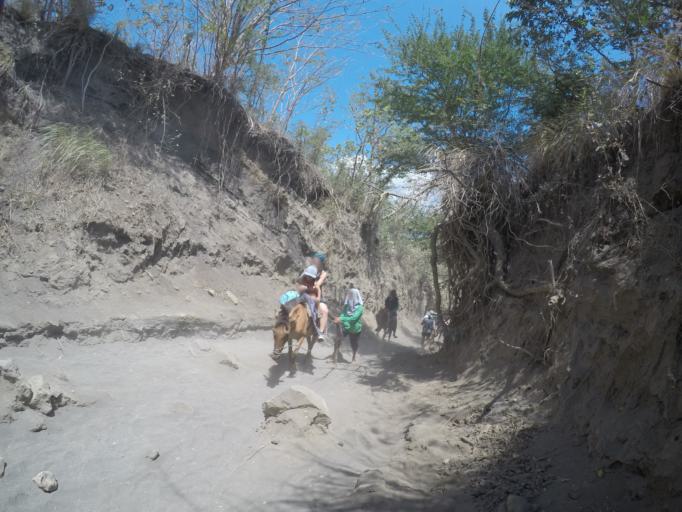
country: PH
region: Calabarzon
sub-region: Province of Batangas
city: Sampaloc
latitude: 14.0310
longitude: 121.0005
